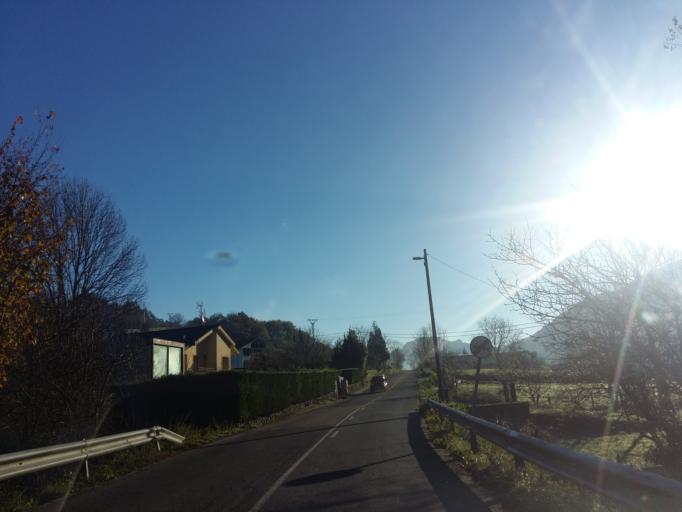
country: ES
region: Cantabria
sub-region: Provincia de Cantabria
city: Ramales de la Victoria
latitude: 43.2777
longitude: -3.5244
